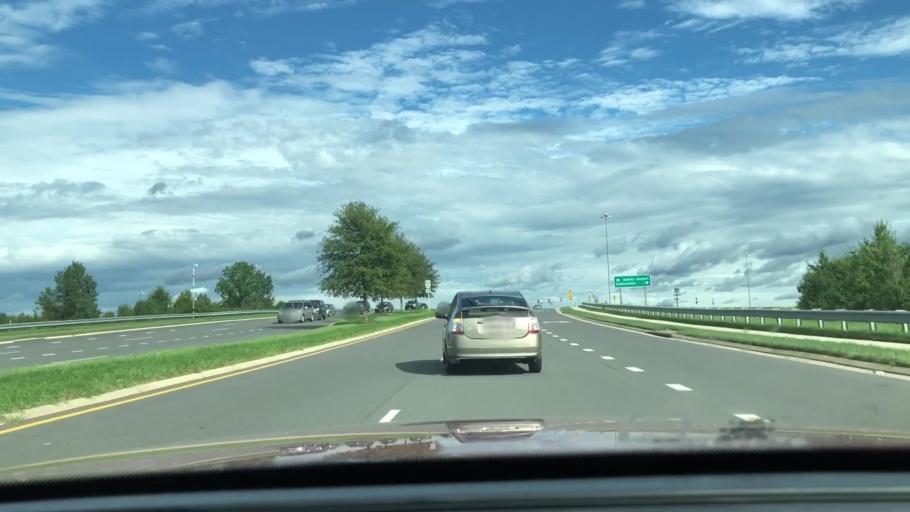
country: US
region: Virginia
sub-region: Fairfax County
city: Chantilly
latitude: 38.8868
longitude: -77.4506
